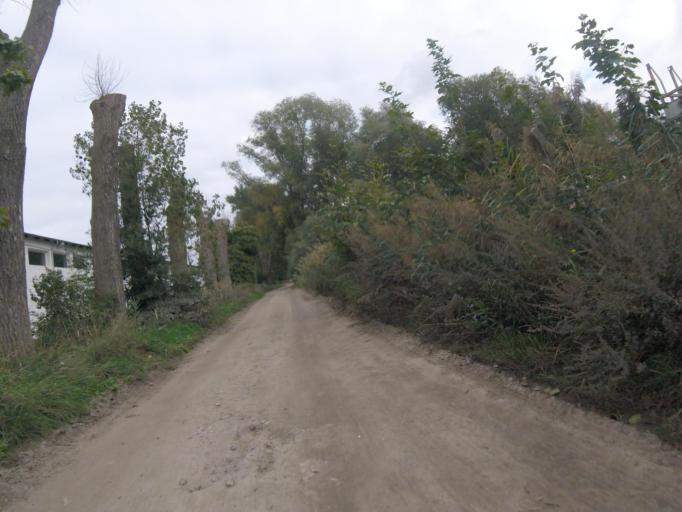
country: DE
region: Brandenburg
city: Mittenwalde
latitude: 52.2694
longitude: 13.5400
